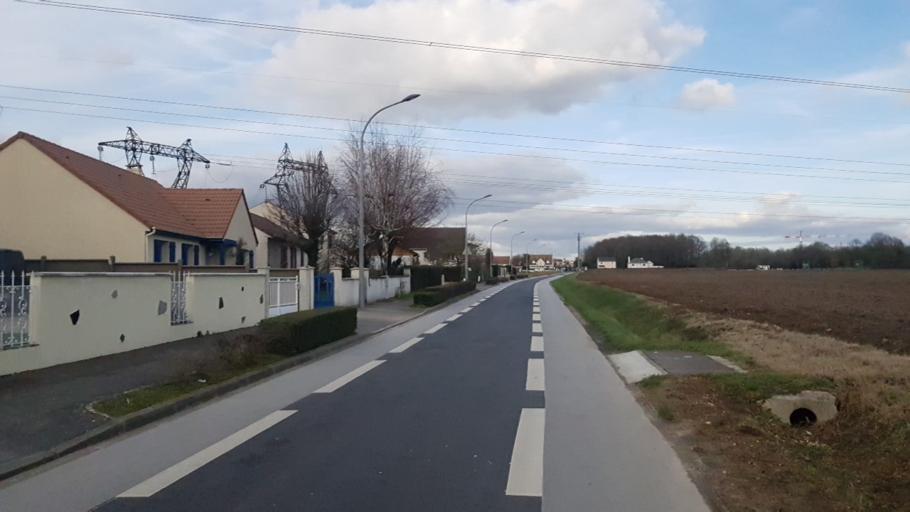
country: FR
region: Ile-de-France
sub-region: Departement de l'Essonne
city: Cheptainville
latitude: 48.5517
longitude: 2.2796
